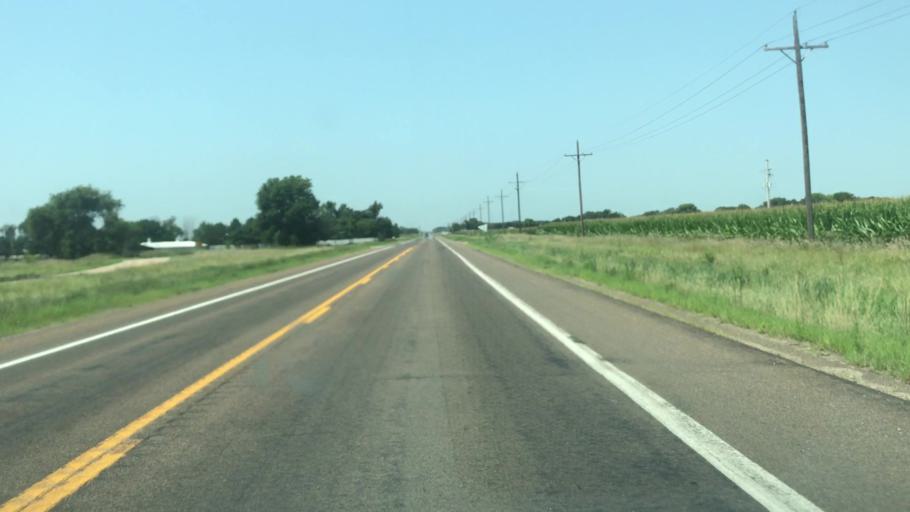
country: US
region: Nebraska
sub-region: Hall County
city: Grand Island
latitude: 40.8869
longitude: -98.3239
